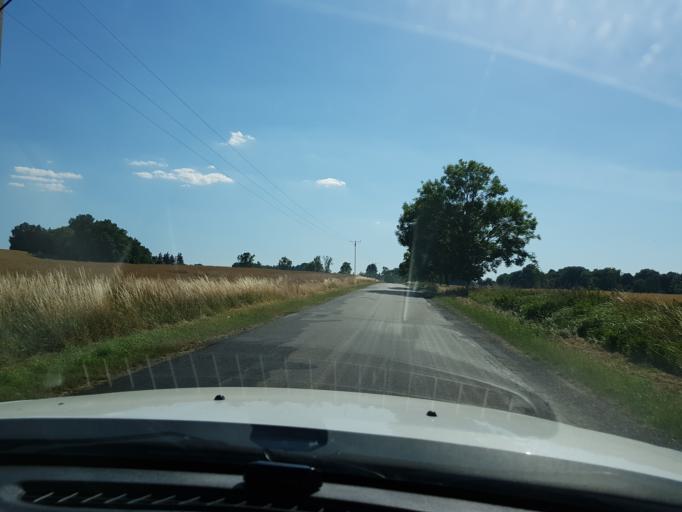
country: PL
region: West Pomeranian Voivodeship
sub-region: Powiat bialogardzki
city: Karlino
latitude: 53.9456
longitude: 15.8531
